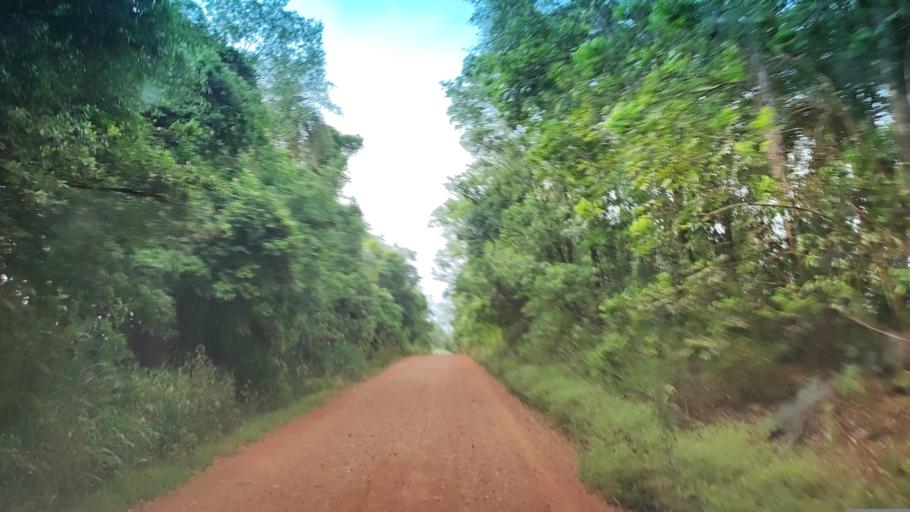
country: AR
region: Misiones
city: Gobernador Roca
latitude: -27.1698
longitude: -55.5095
